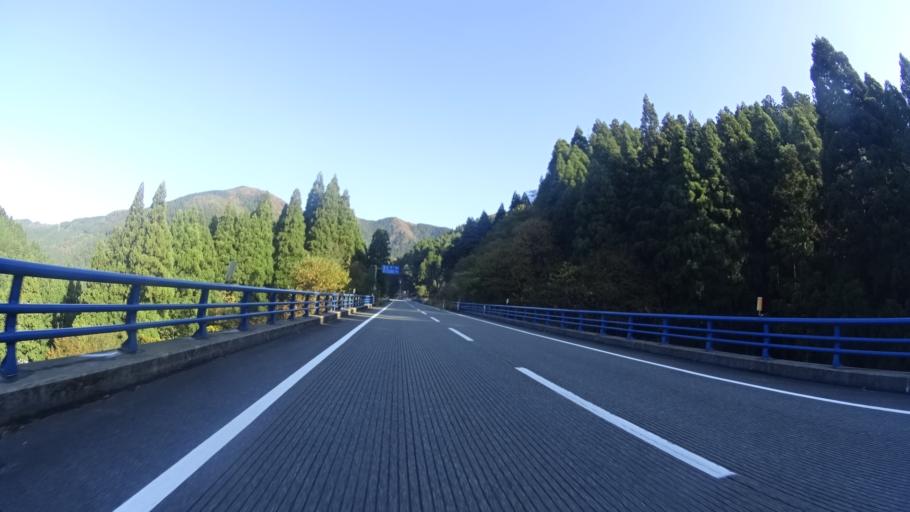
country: JP
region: Fukui
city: Maruoka
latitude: 36.1689
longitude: 136.3325
